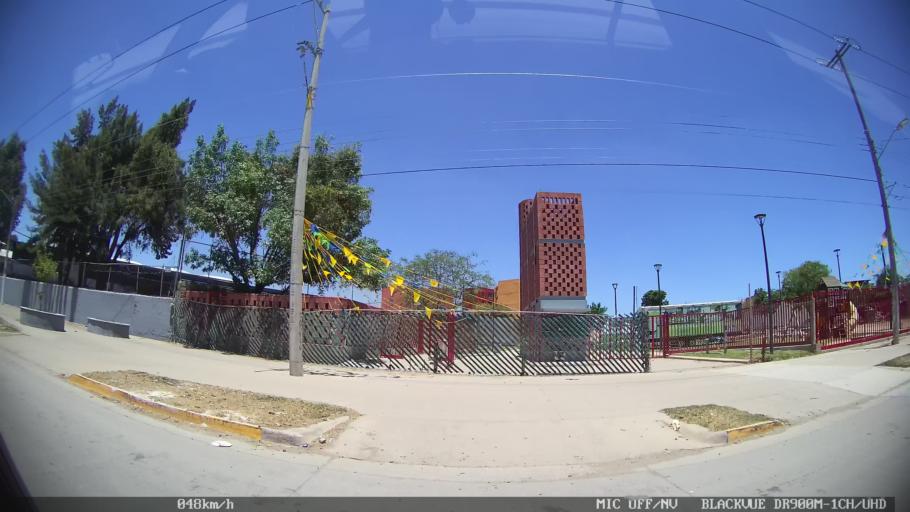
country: MX
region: Jalisco
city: Tlaquepaque
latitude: 20.6729
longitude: -103.2699
